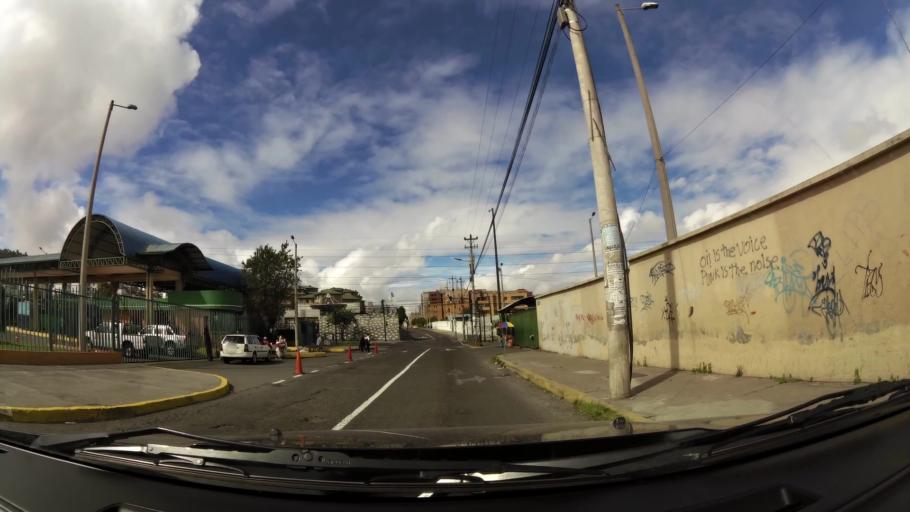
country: EC
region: Pichincha
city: Quito
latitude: -0.1635
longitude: -78.4715
